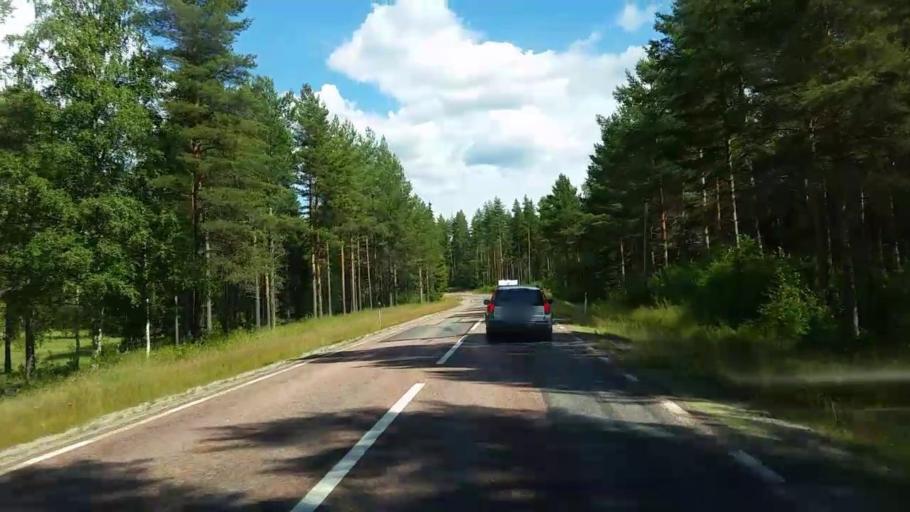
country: SE
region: Gaevleborg
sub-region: Ovanakers Kommun
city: Edsbyn
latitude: 61.3452
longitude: 15.6656
